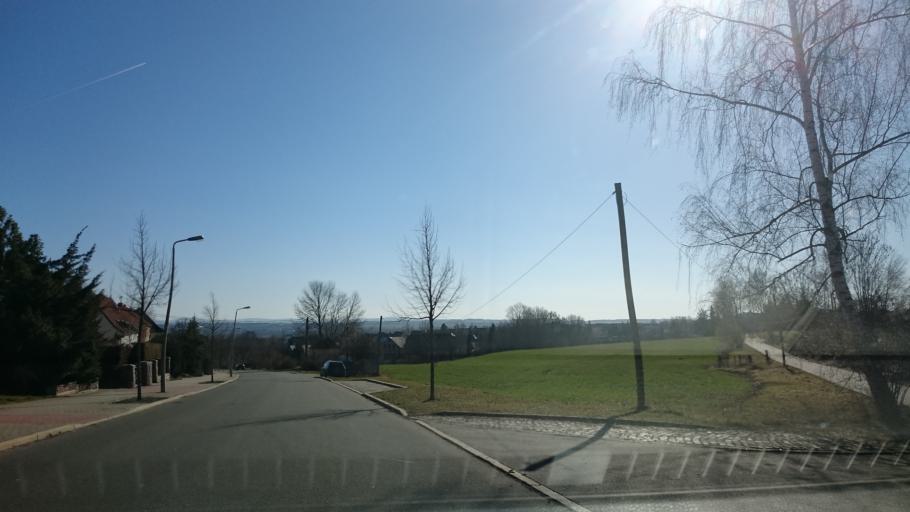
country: DE
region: Saxony
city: Lichtentanne
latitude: 50.7293
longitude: 12.4394
